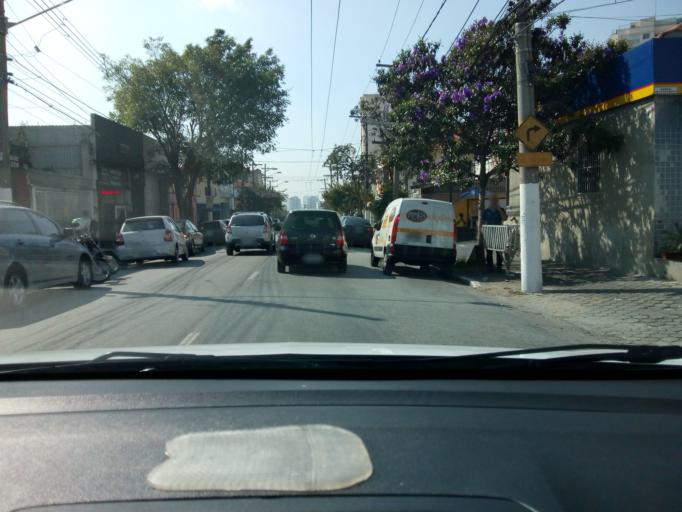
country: BR
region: Sao Paulo
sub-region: Sao Paulo
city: Sao Paulo
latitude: -23.5783
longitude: -46.6211
